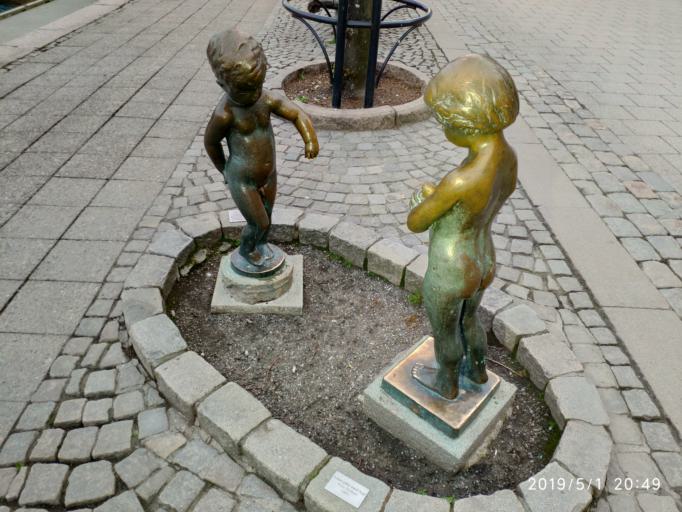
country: NO
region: Aust-Agder
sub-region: Arendal
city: Arendal
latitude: 58.4601
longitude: 8.7672
